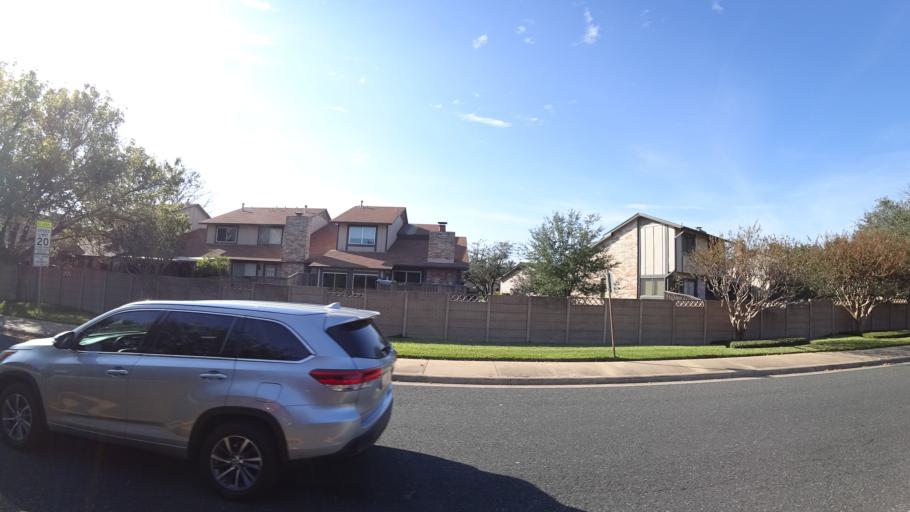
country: US
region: Texas
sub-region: Williamson County
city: Anderson Mill
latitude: 30.4552
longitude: -97.8072
